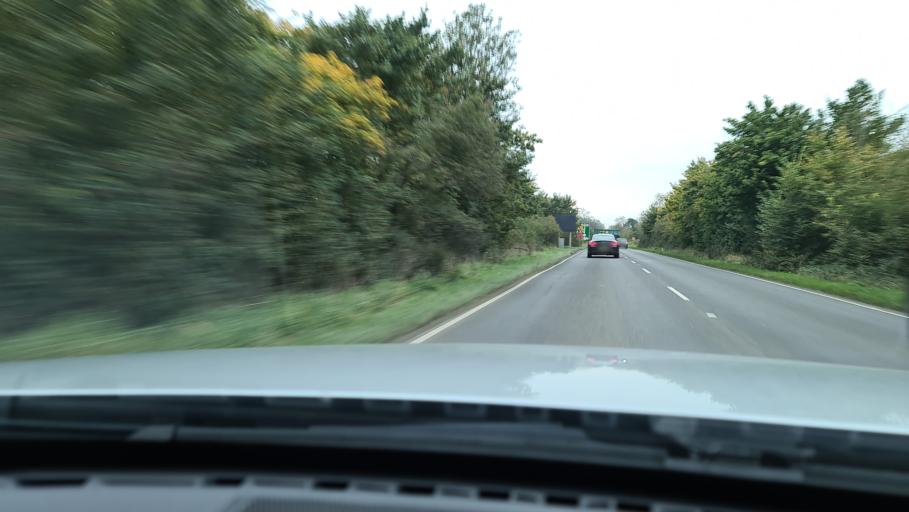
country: GB
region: England
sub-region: Oxfordshire
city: Bicester
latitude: 51.8763
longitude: -1.0876
